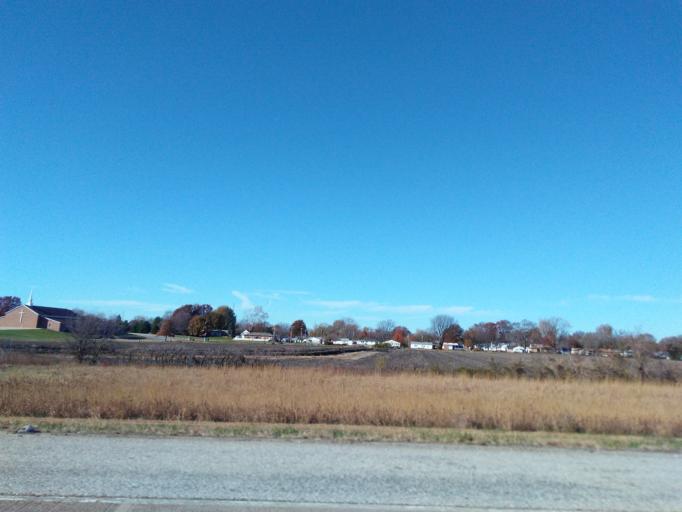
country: US
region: Illinois
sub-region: Saint Clair County
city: Dupo
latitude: 38.5210
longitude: -90.1998
